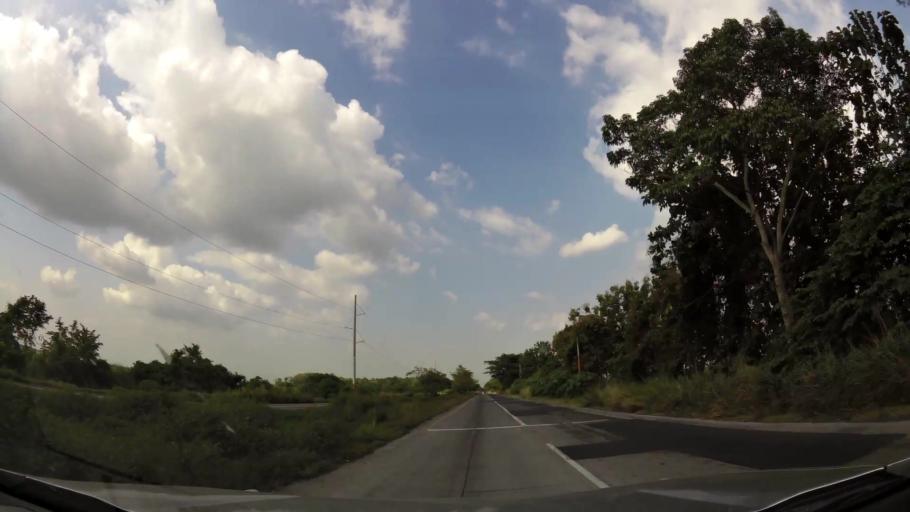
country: GT
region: Escuintla
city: Puerto San Jose
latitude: 14.0390
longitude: -90.7791
